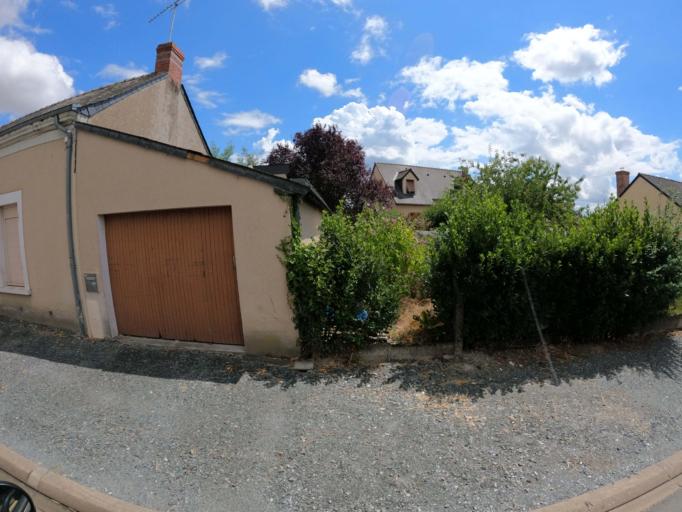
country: FR
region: Pays de la Loire
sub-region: Departement de Maine-et-Loire
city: Mire
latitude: 47.7592
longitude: -0.4892
